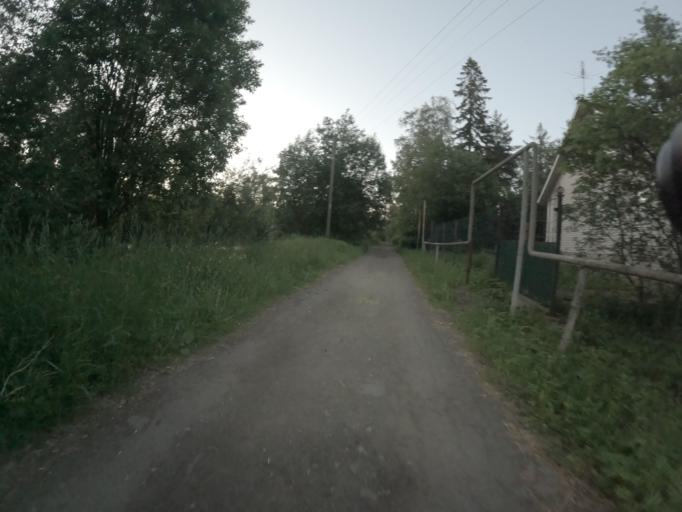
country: RU
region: Leningrad
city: Vsevolozhsk
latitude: 60.0137
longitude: 30.6112
